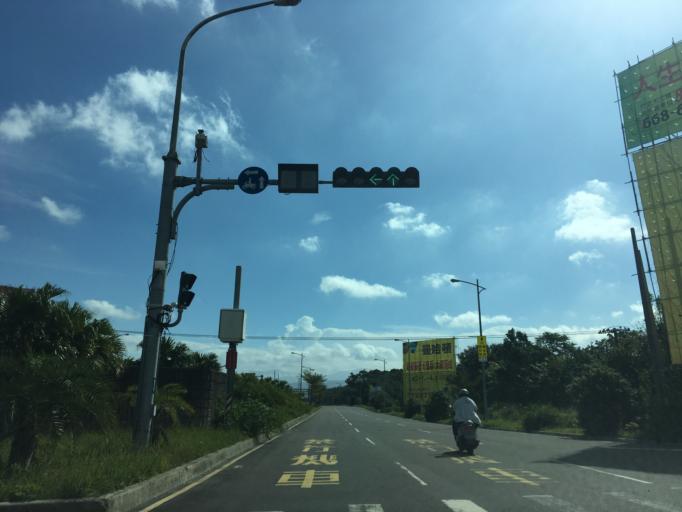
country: TW
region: Taiwan
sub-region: Hsinchu
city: Zhubei
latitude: 24.7957
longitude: 121.0133
